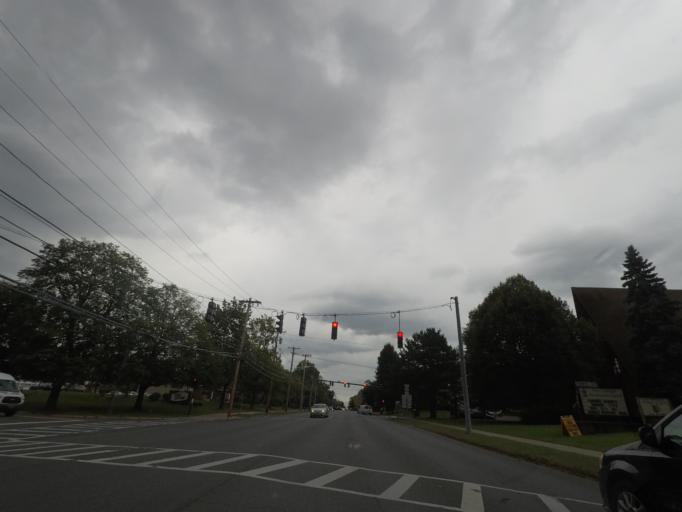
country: US
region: New York
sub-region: Albany County
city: Roessleville
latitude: 42.6724
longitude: -73.8105
